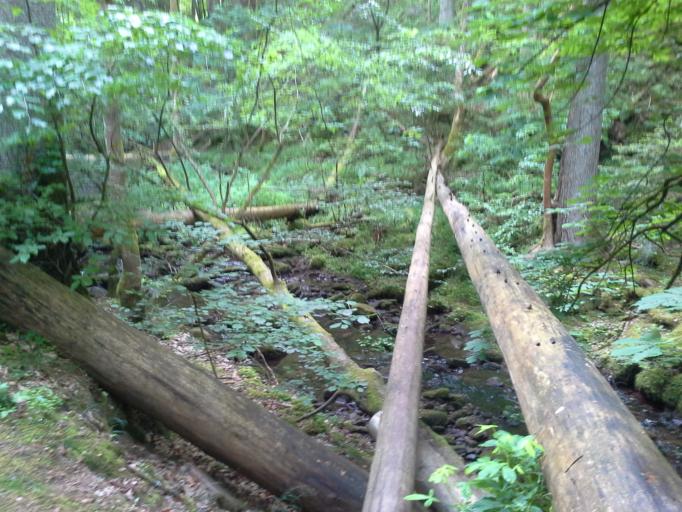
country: DE
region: Baden-Wuerttemberg
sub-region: Karlsruhe Region
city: Bad Liebenzell
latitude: 48.8026
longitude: 8.7418
